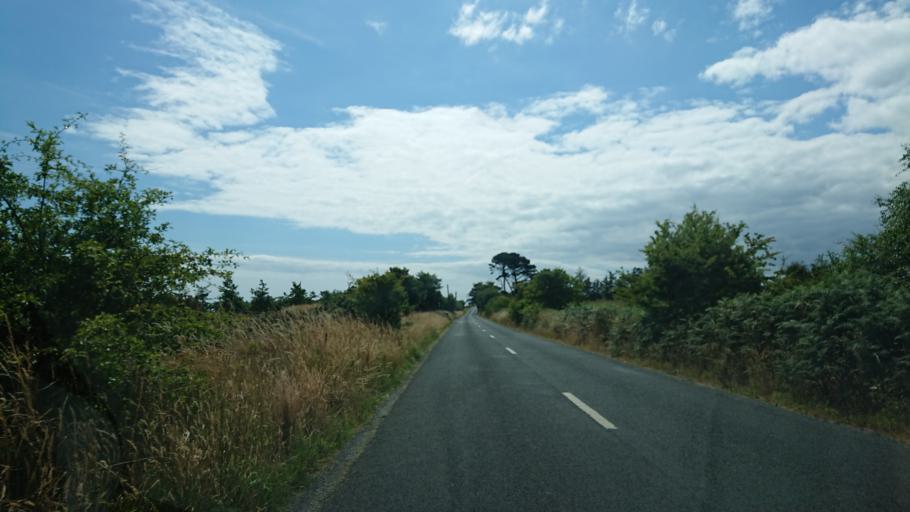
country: IE
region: Munster
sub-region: Waterford
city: Portlaw
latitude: 52.1572
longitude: -7.3438
